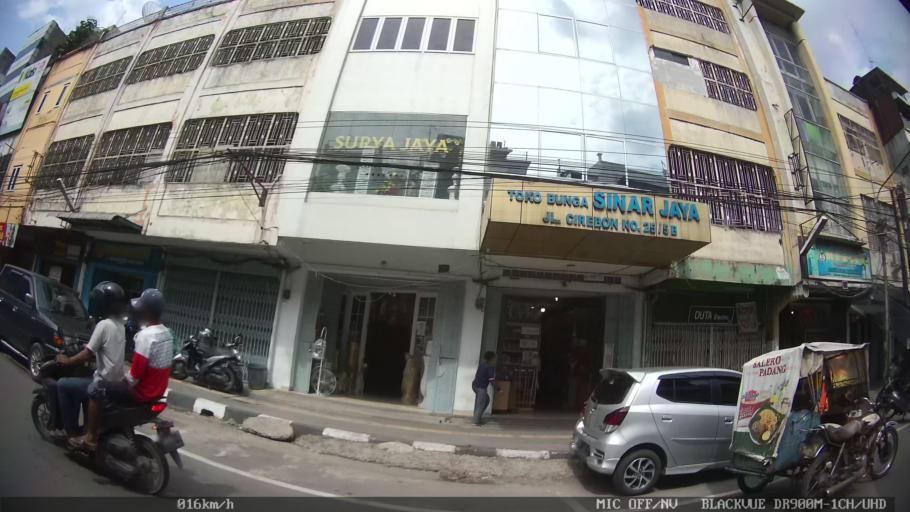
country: ID
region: North Sumatra
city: Medan
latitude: 3.5859
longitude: 98.6835
